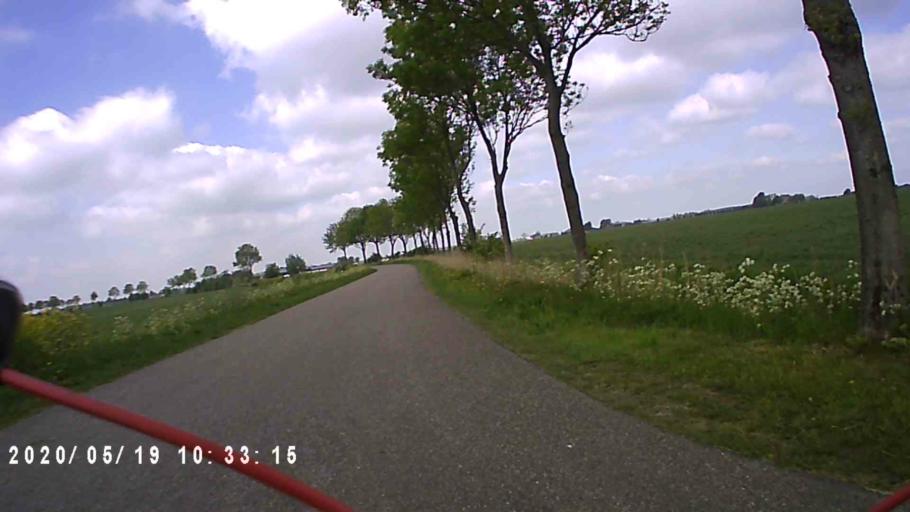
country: NL
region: Friesland
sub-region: Gemeente Kollumerland en Nieuwkruisland
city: Kollum
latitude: 53.2869
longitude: 6.1902
